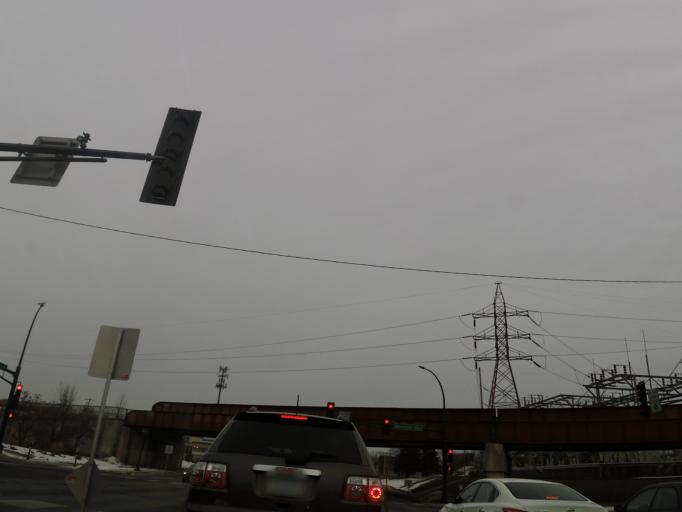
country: US
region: Minnesota
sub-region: Ramsey County
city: Falcon Heights
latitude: 44.9482
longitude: -93.1670
